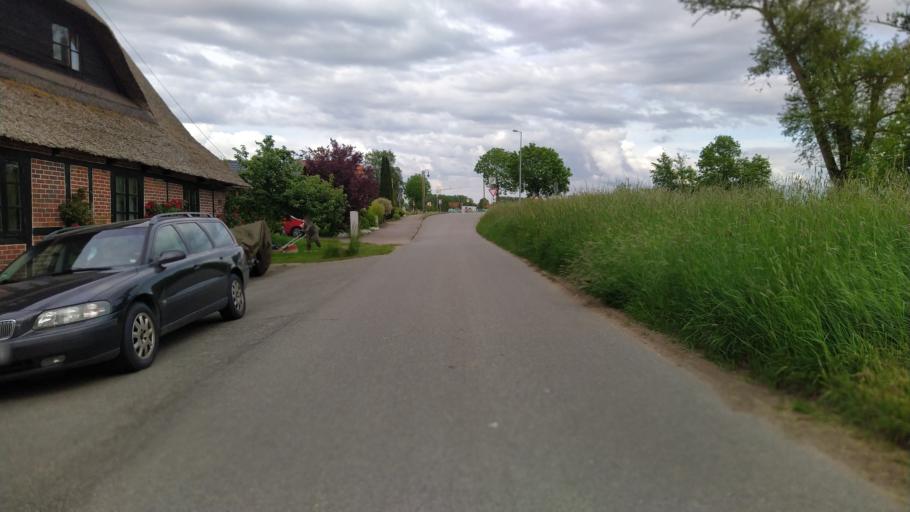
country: DE
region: Lower Saxony
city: Neu Wulmstorf
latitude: 53.4906
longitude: 9.7474
